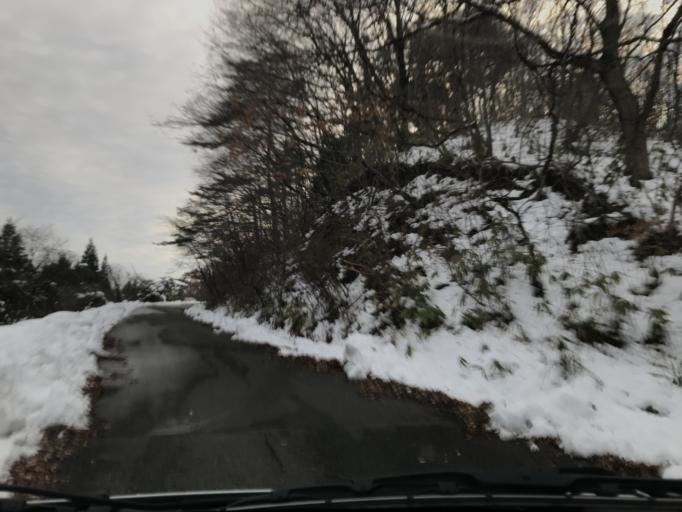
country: JP
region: Iwate
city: Mizusawa
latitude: 39.0412
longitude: 141.0306
